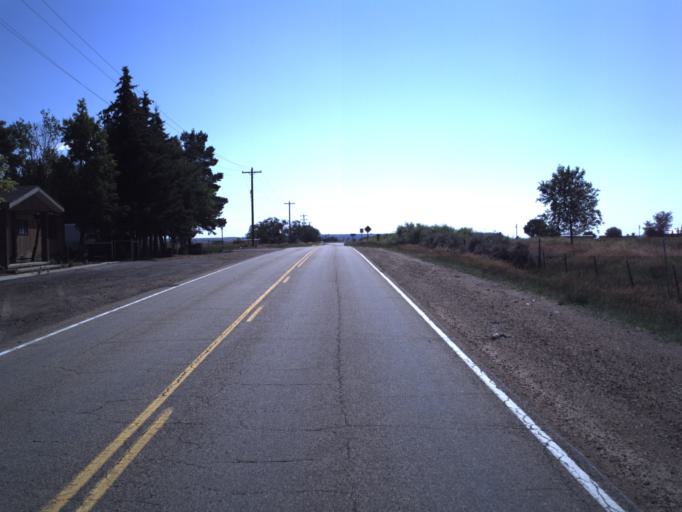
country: US
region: Utah
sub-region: Duchesne County
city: Duchesne
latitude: 40.3593
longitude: -110.2813
